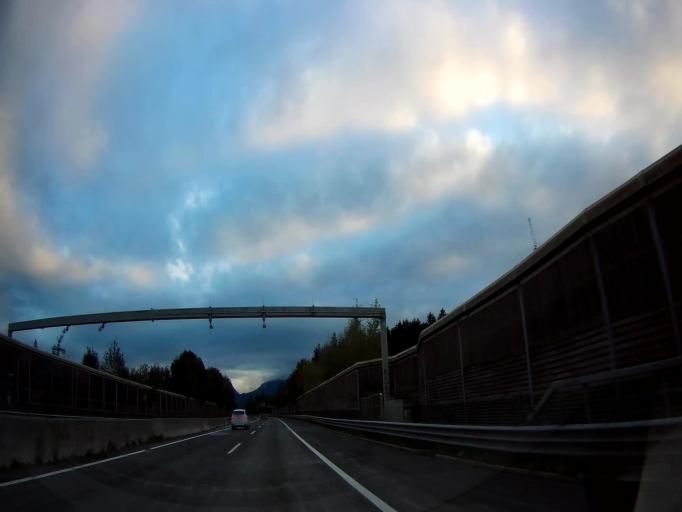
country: AT
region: Salzburg
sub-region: Politischer Bezirk Hallein
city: Adnet
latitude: 47.6631
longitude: 13.1297
